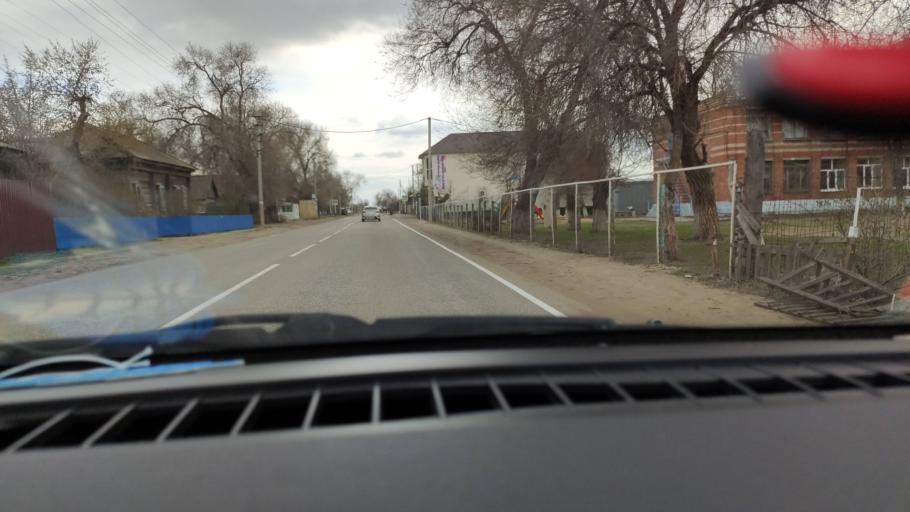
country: RU
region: Saratov
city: Privolzhskiy
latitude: 51.1832
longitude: 45.9187
